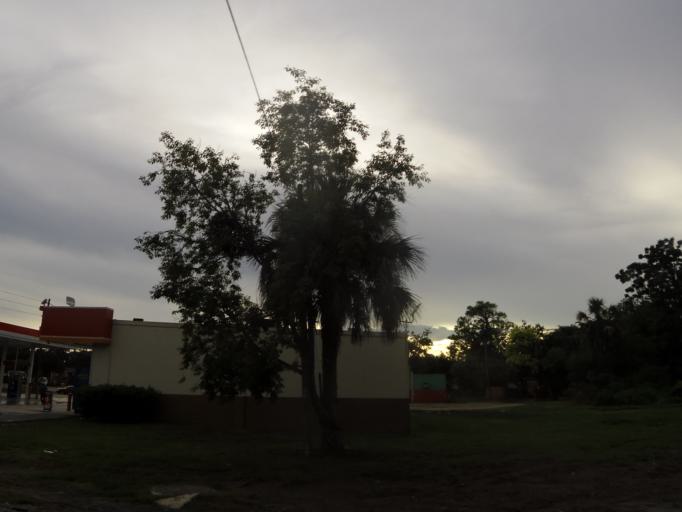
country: US
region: Florida
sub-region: Duval County
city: Neptune Beach
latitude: 30.2878
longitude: -81.5012
